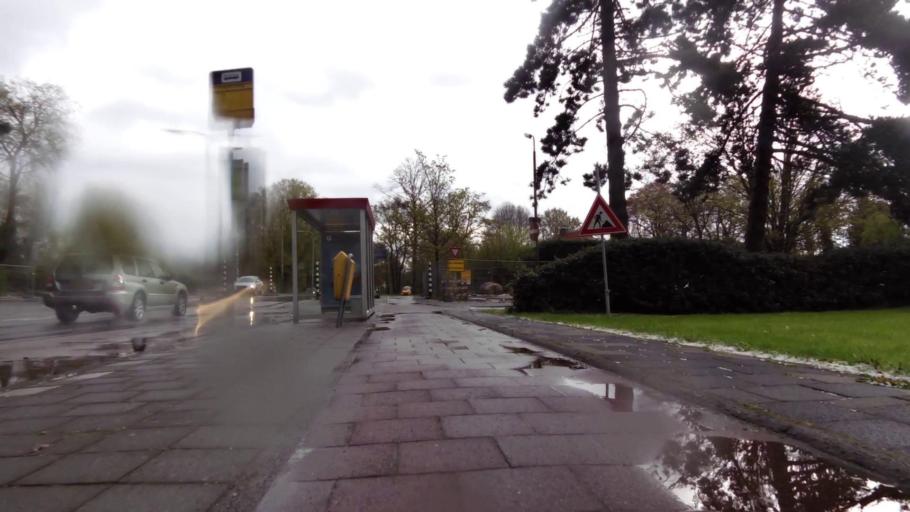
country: NL
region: North Holland
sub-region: Gemeente Velsen
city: Velsen-Zuid
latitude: 52.4510
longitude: 4.6325
